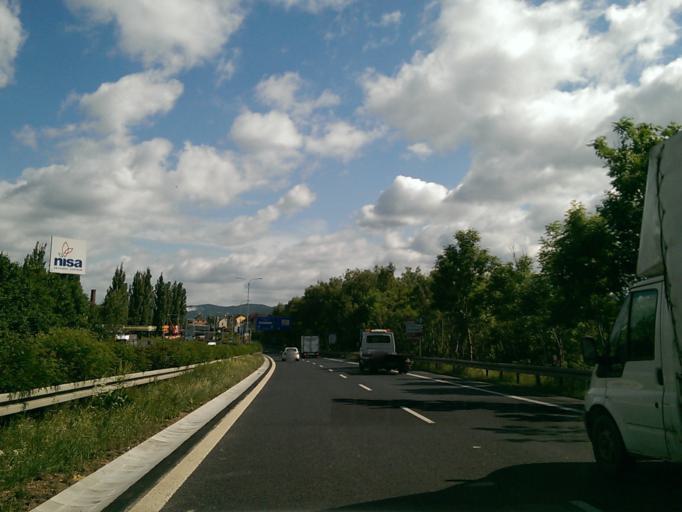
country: CZ
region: Liberecky
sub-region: Okres Liberec
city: Liberec
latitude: 50.7407
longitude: 15.0529
